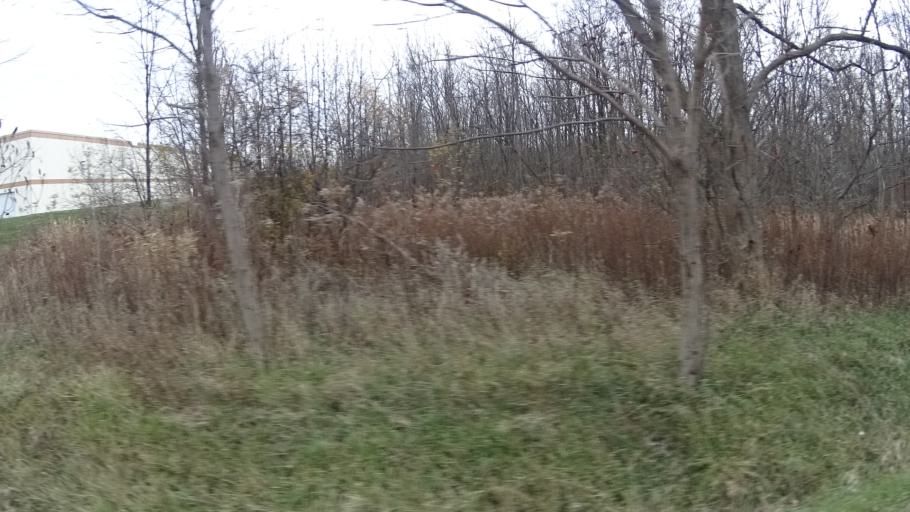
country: US
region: Ohio
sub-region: Cuyahoga County
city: Strongsville
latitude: 41.2923
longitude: -81.8779
